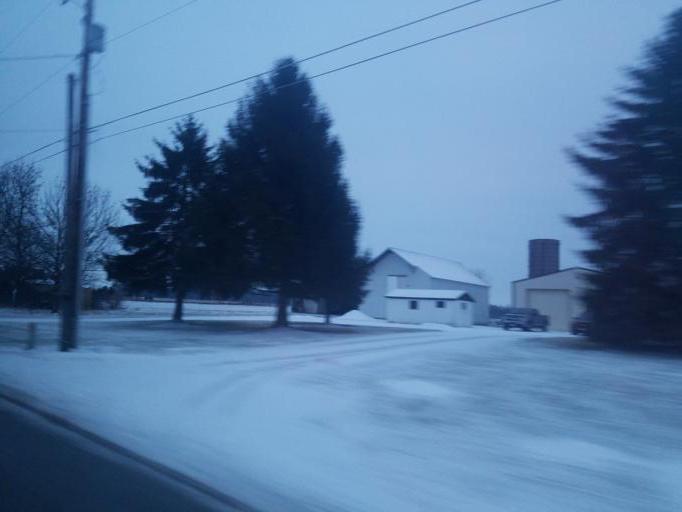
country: US
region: Ohio
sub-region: Delaware County
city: Sunbury
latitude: 40.2052
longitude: -82.8453
